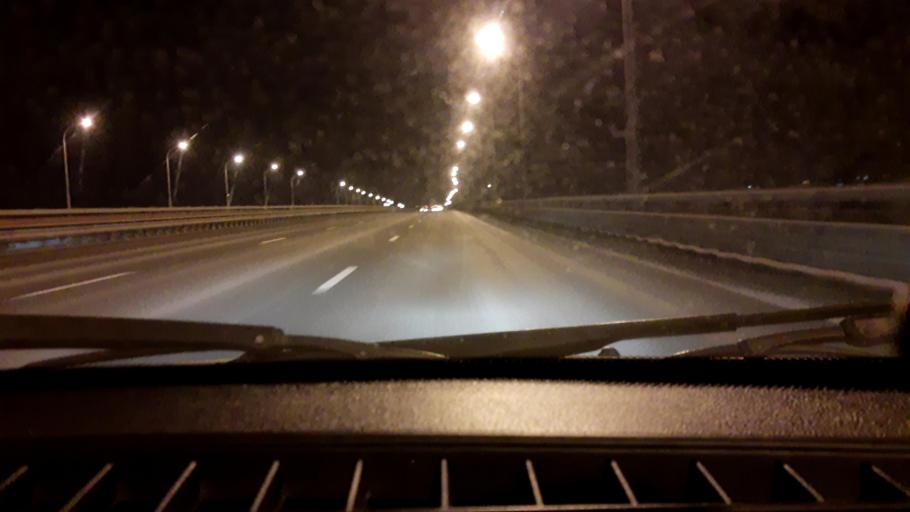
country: RU
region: Bashkortostan
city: Ufa
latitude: 54.6447
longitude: 56.0003
